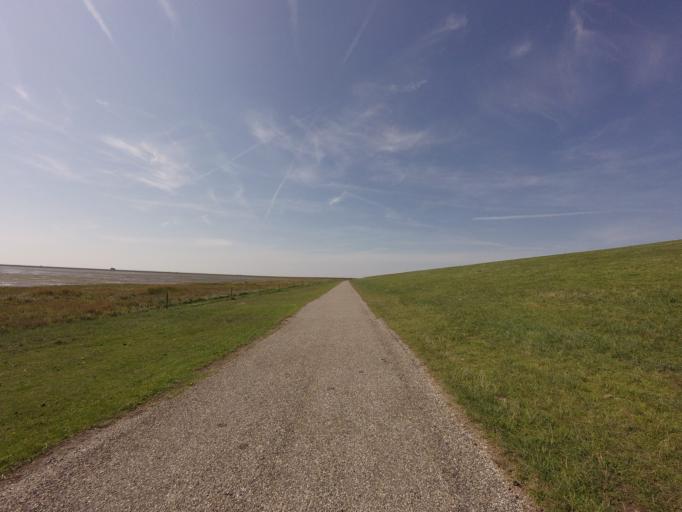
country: NL
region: Friesland
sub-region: Gemeente Schiermonnikoog
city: Schiermonnikoog
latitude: 53.4741
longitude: 6.2025
